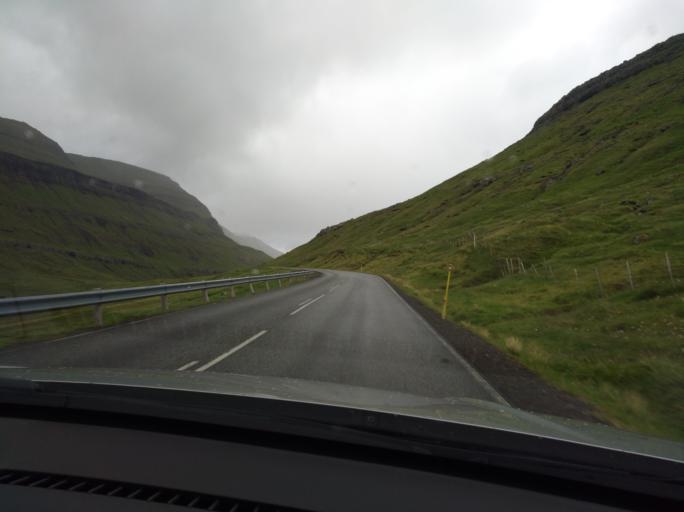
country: FO
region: Eysturoy
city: Fuglafjordur
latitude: 62.2285
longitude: -6.8790
